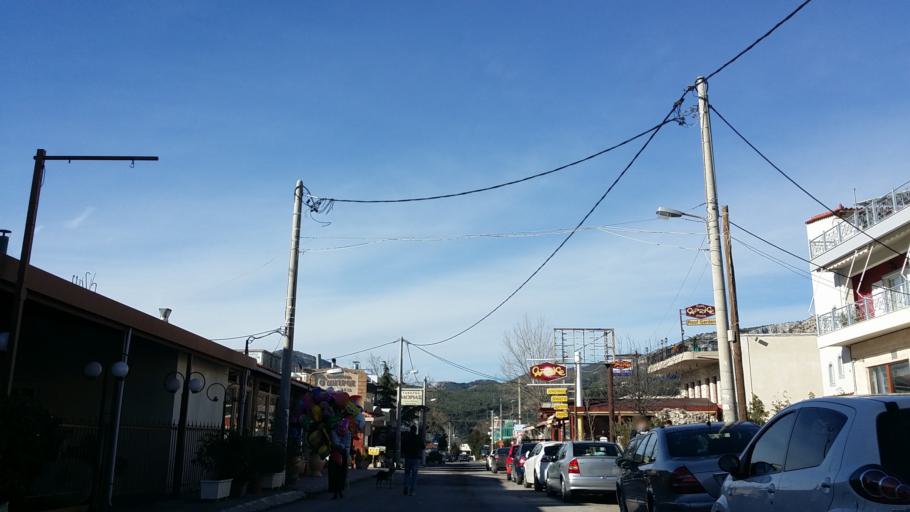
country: GR
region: Attica
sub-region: Nomarchia Dytikis Attikis
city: Fyli
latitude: 38.1057
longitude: 23.6685
